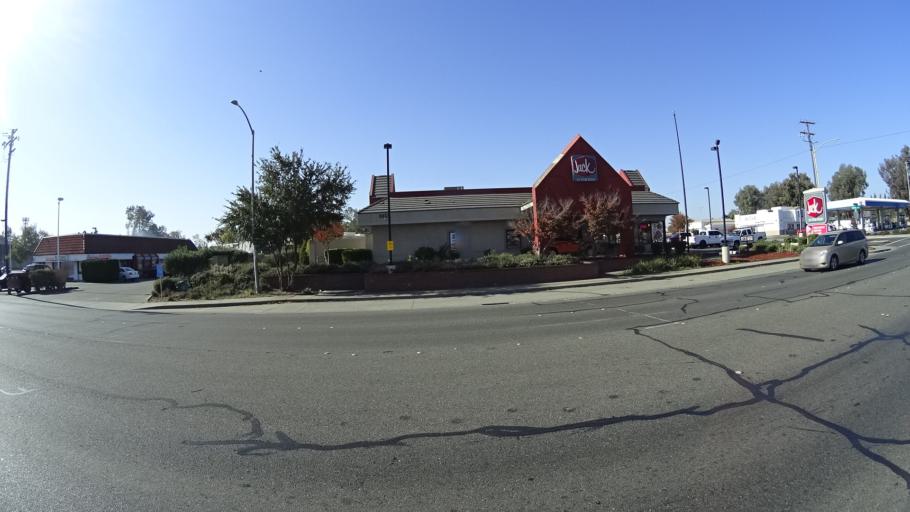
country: US
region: California
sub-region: Sacramento County
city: Citrus Heights
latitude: 38.7216
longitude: -121.2904
